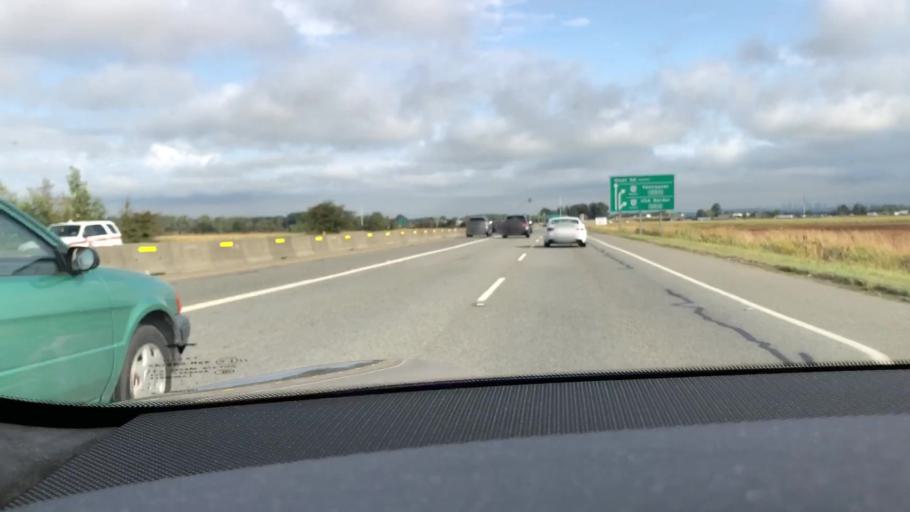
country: CA
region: British Columbia
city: Ladner
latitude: 49.0977
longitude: -123.0574
